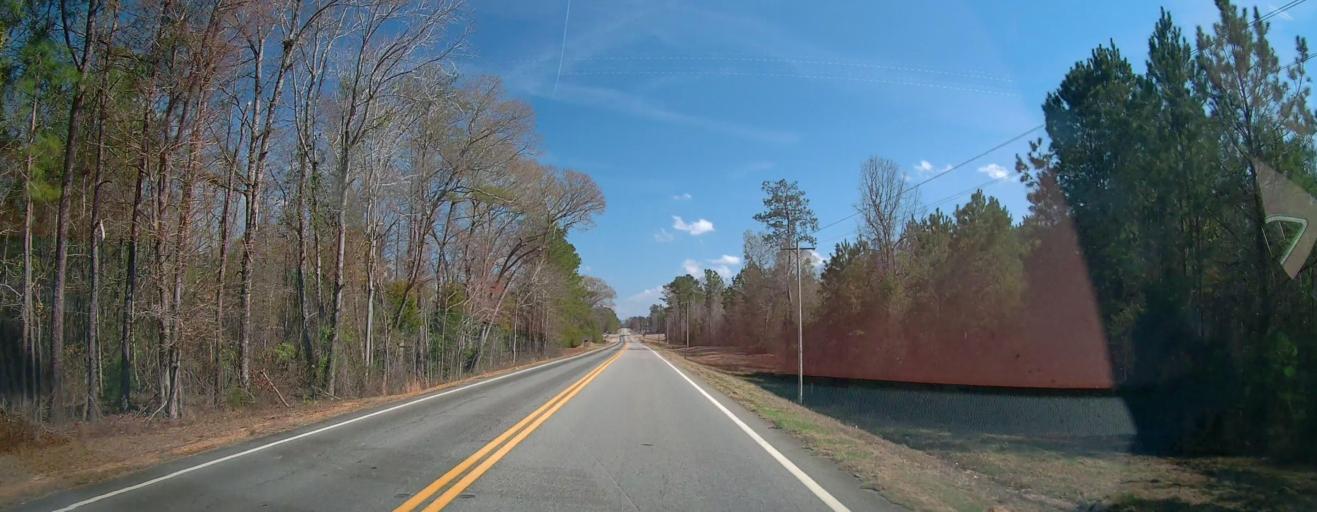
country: US
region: Georgia
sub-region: Wilkinson County
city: Gordon
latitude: 32.8970
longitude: -83.3644
